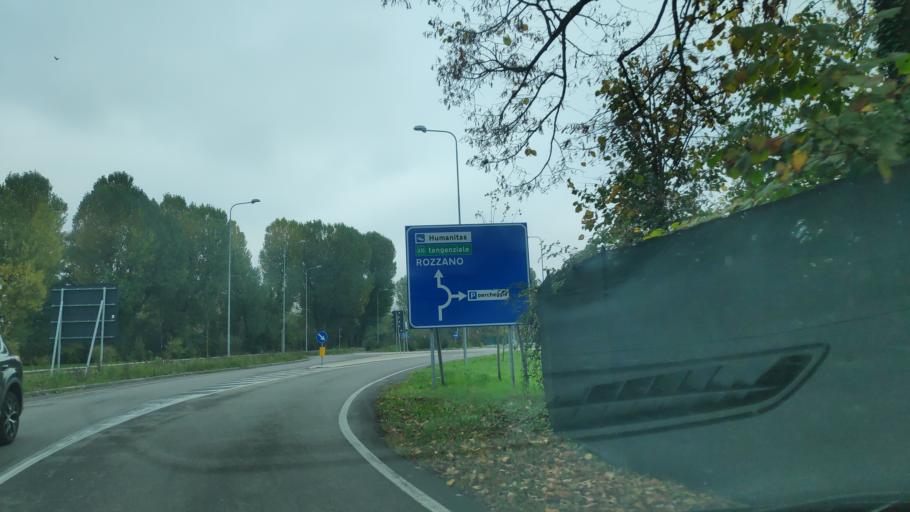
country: IT
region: Lombardy
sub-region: Citta metropolitana di Milano
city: Basiglio
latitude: 45.3693
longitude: 9.1669
